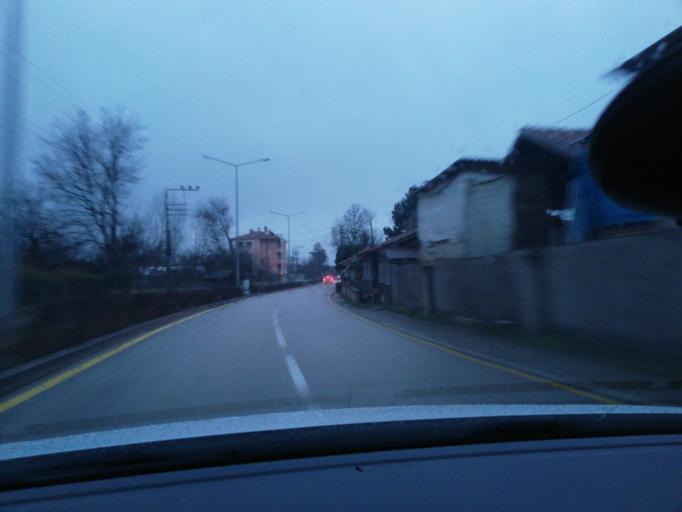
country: TR
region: Bolu
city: Bolu
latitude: 40.7308
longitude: 31.5724
